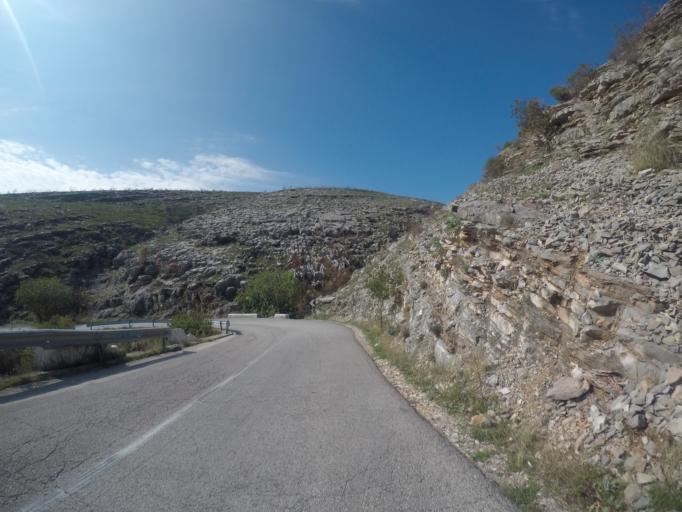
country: AL
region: Gjirokaster
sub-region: Rrethi i Gjirokastres
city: Libohove
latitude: 39.9448
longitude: 20.2563
